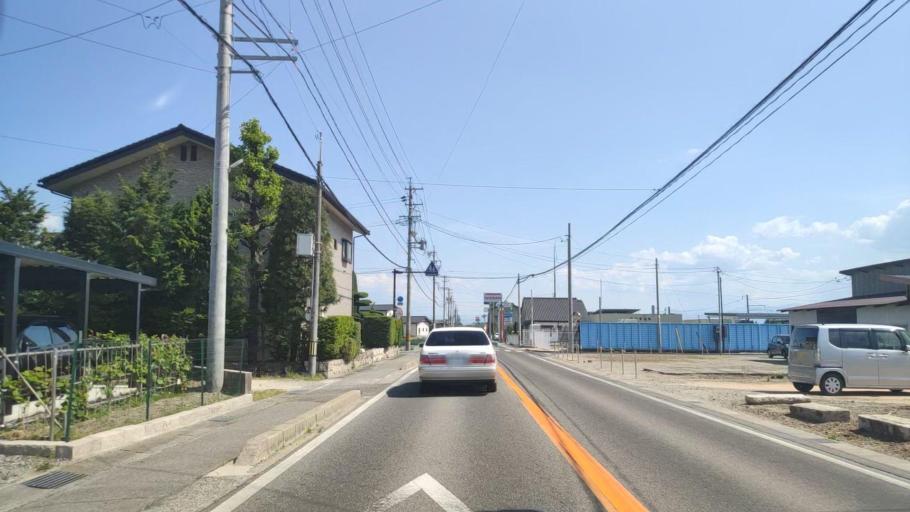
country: JP
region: Nagano
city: Hotaka
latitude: 36.3652
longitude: 137.8768
